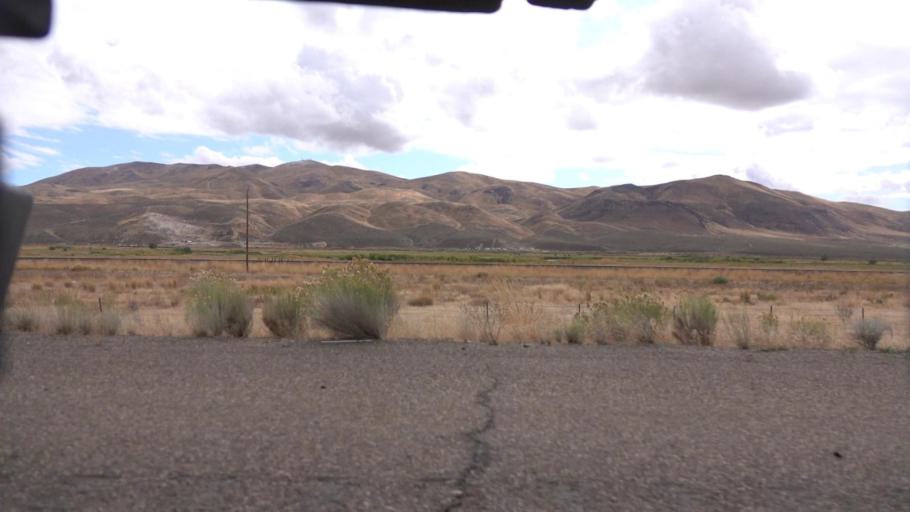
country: US
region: Nevada
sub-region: Elko County
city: Elko
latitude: 40.9196
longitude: -115.6864
